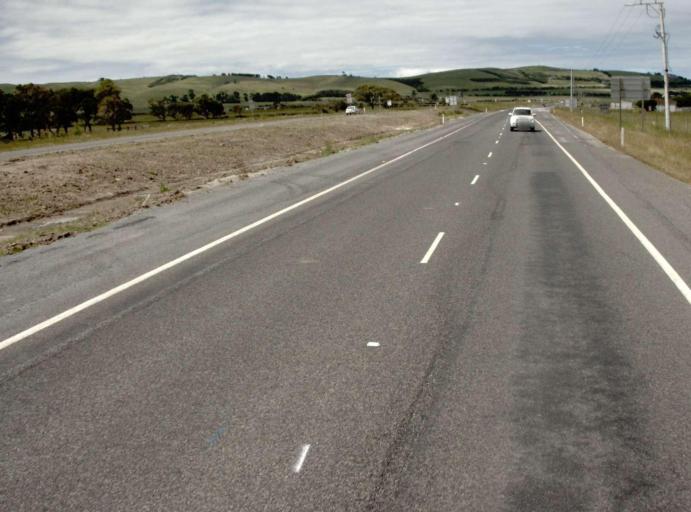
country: AU
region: Victoria
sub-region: Bass Coast
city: North Wonthaggi
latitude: -38.4905
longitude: 145.4634
